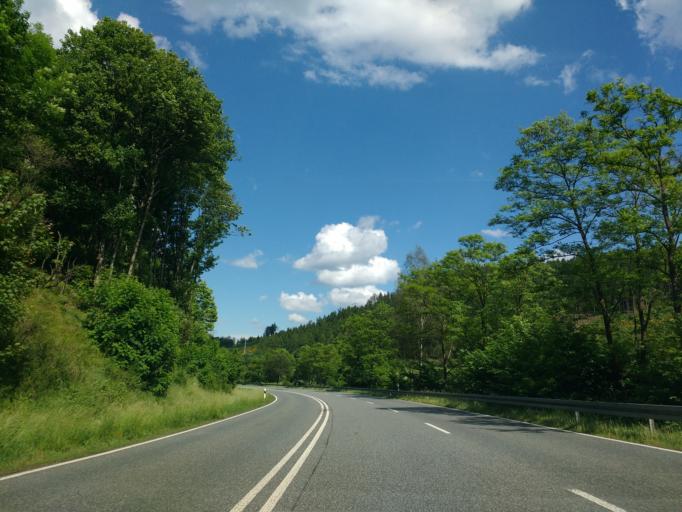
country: DE
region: Hesse
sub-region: Regierungsbezirk Giessen
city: Breidenbach
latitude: 50.8740
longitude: 8.4485
